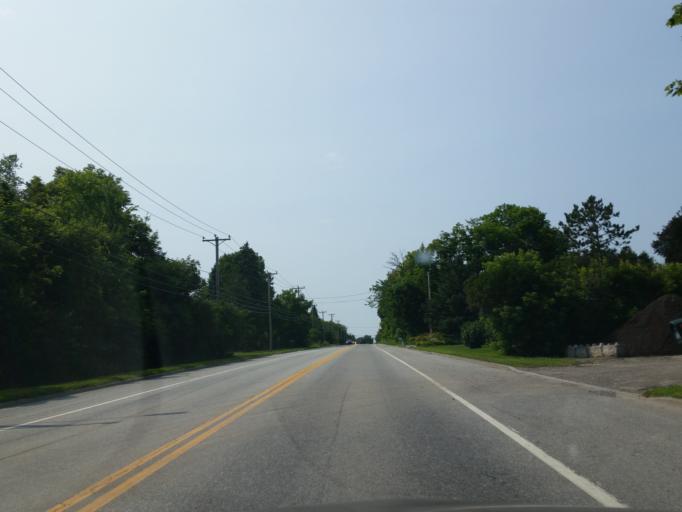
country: CA
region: Ontario
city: Bells Corners
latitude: 45.4122
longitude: -75.8737
